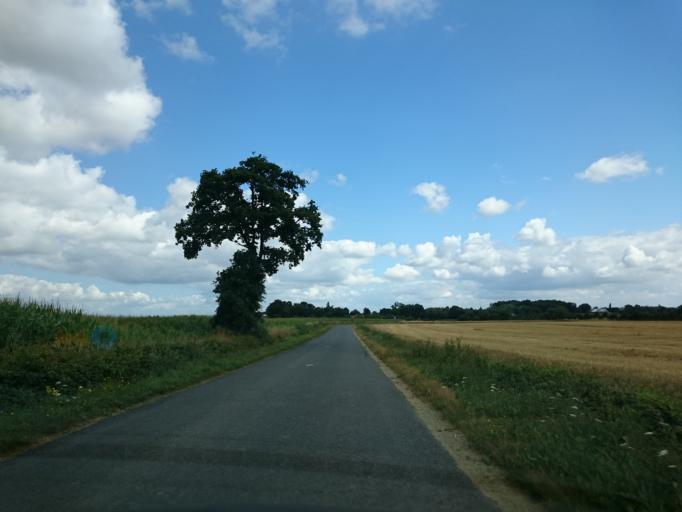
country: FR
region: Brittany
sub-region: Departement d'Ille-et-Vilaine
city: Chanteloup
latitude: 47.9534
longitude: -1.6412
